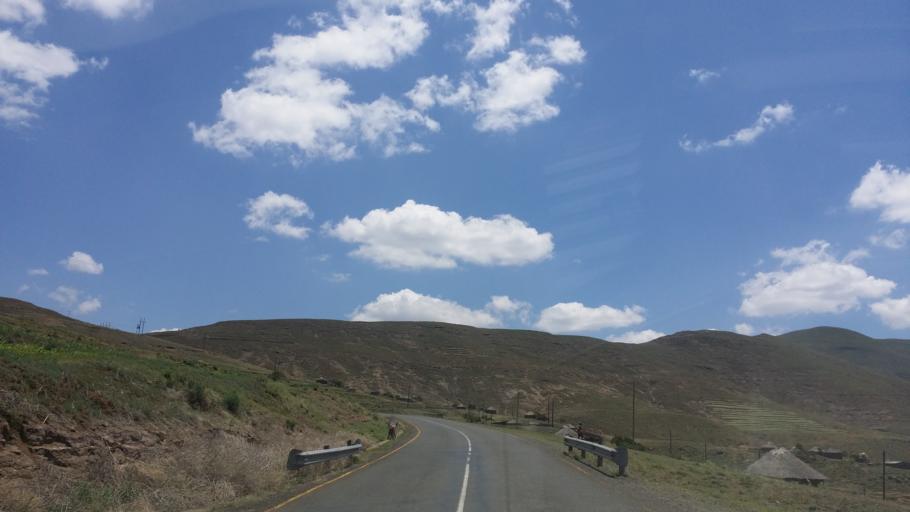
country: LS
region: Mokhotlong
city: Mokhotlong
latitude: -29.2671
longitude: 28.9056
